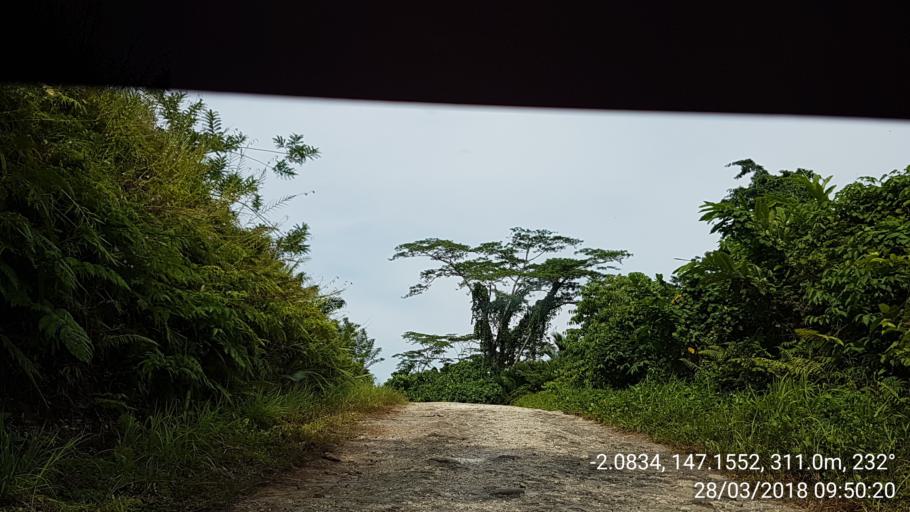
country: PG
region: Manus
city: Lorengau
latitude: -2.0833
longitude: 147.1553
